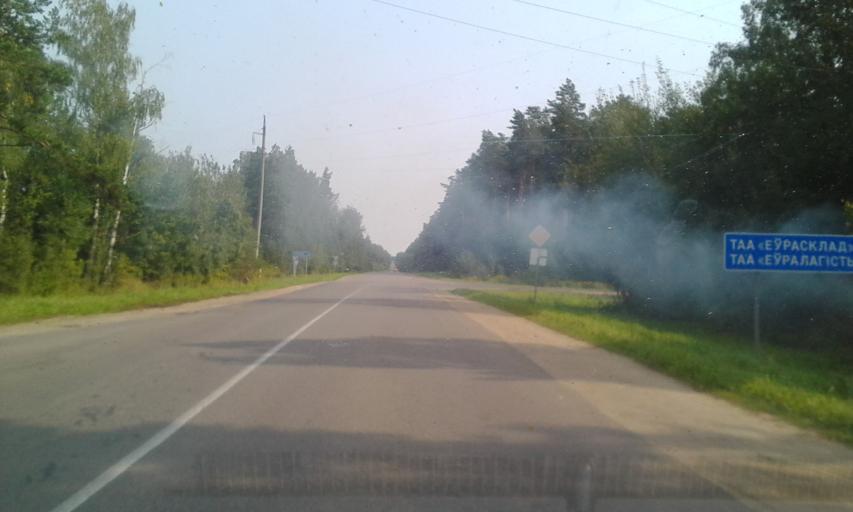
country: BY
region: Minsk
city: Hatava
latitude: 53.7715
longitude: 27.6584
